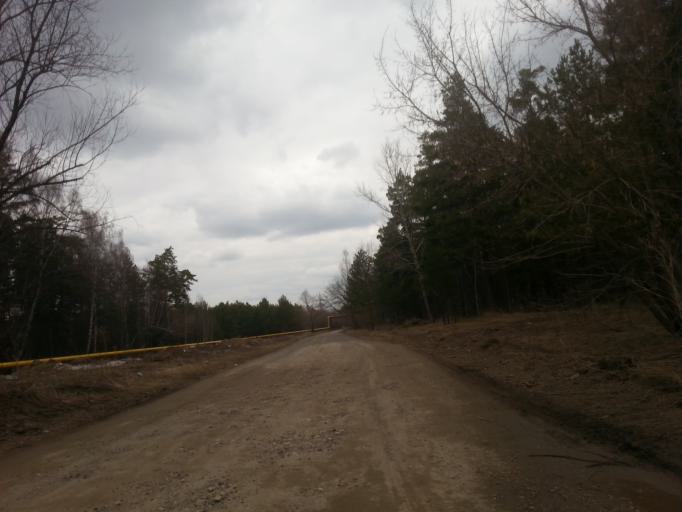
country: RU
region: Altai Krai
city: Yuzhnyy
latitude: 53.2837
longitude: 83.7320
